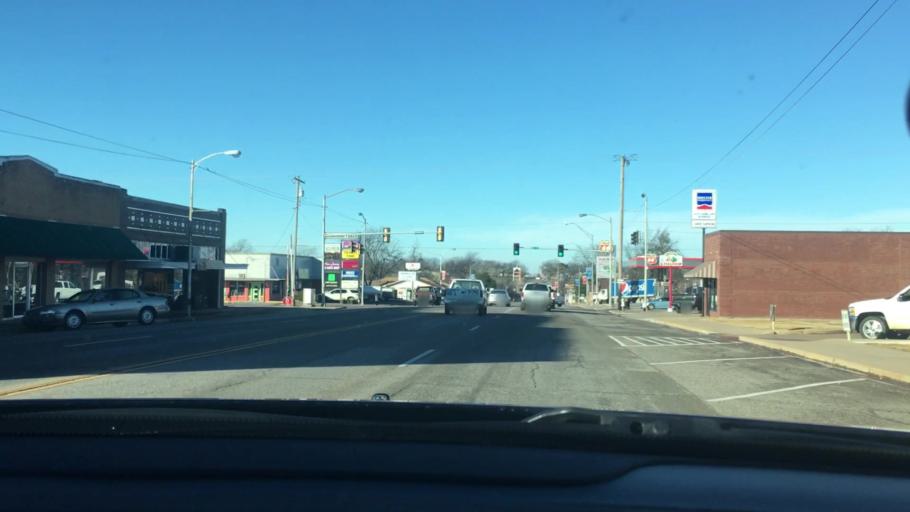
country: US
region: Oklahoma
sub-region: Murray County
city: Sulphur
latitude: 34.5065
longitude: -96.9812
